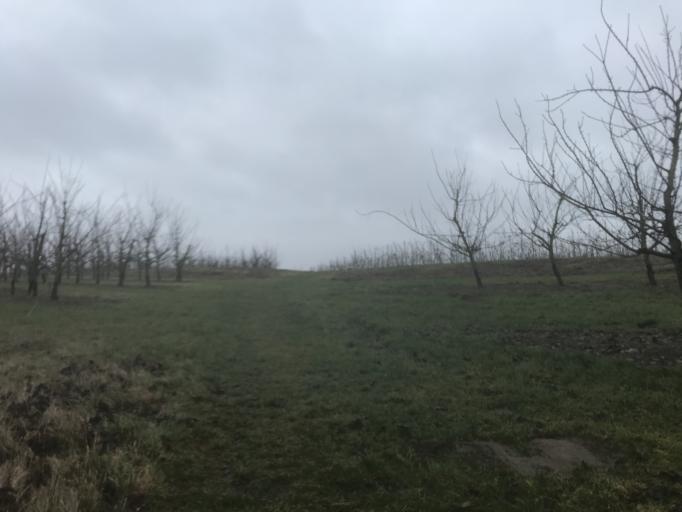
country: DE
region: Rheinland-Pfalz
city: Wackernheim
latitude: 49.9944
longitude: 8.1401
